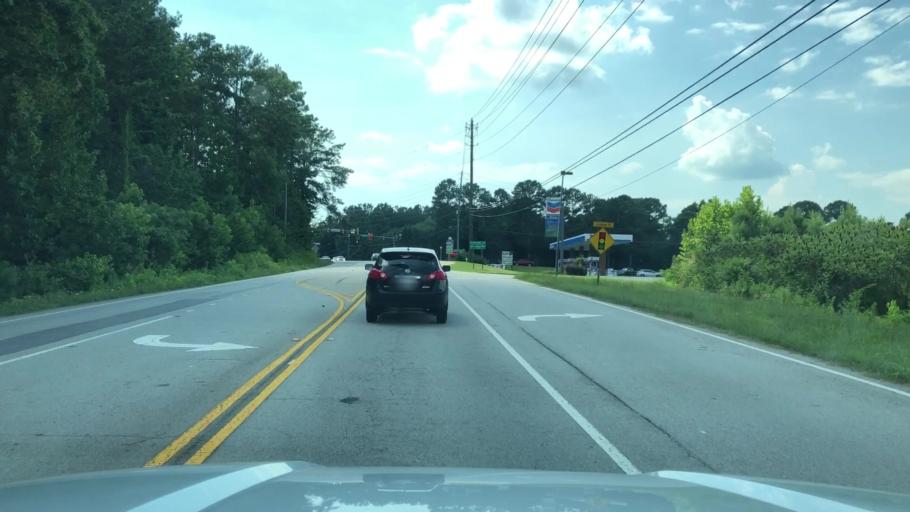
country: US
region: Georgia
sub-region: Paulding County
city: Dallas
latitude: 33.9718
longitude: -84.7997
